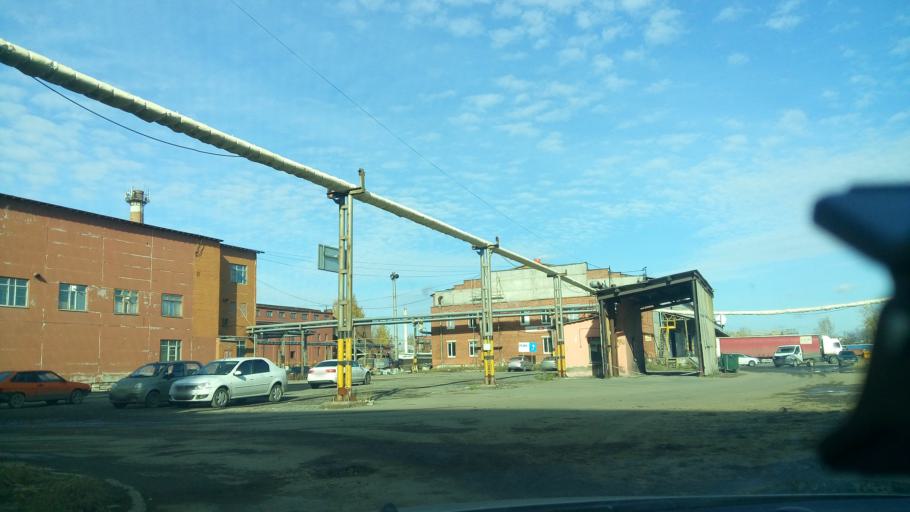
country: RU
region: Sverdlovsk
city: Sovkhoznyy
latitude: 56.7783
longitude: 60.6168
